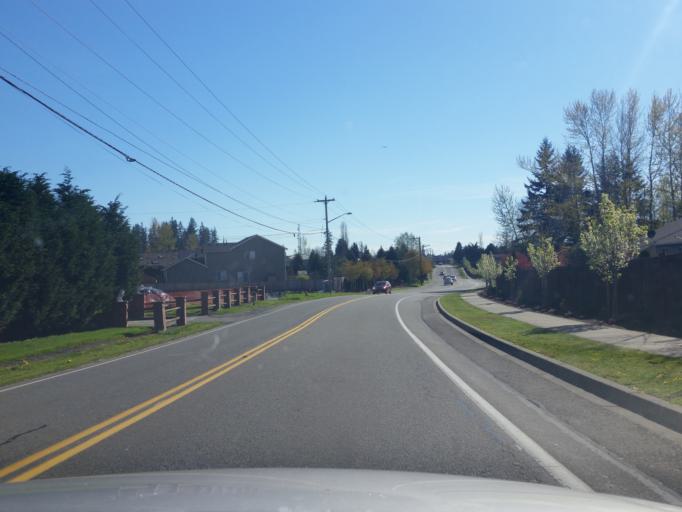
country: US
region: Washington
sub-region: Snohomish County
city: Silver Firs
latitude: 47.8686
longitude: -122.1759
